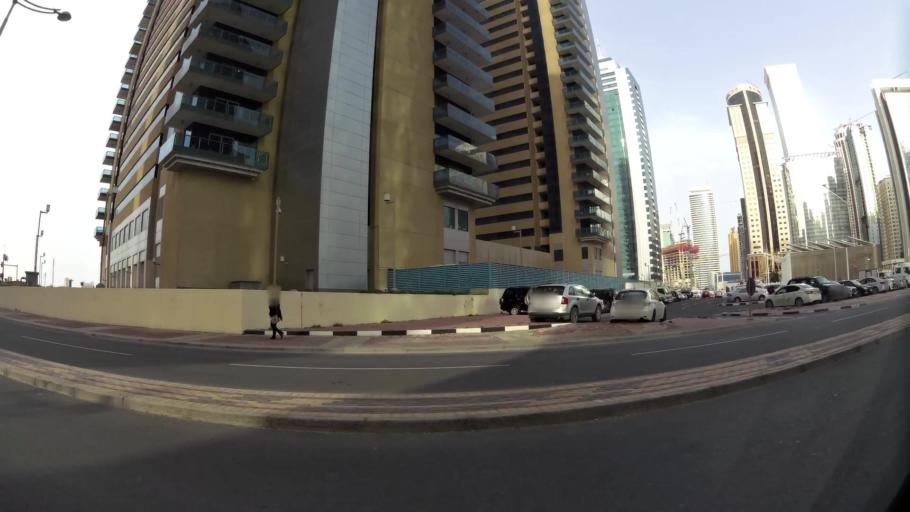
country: QA
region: Baladiyat ad Dawhah
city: Doha
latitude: 25.3296
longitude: 51.5258
